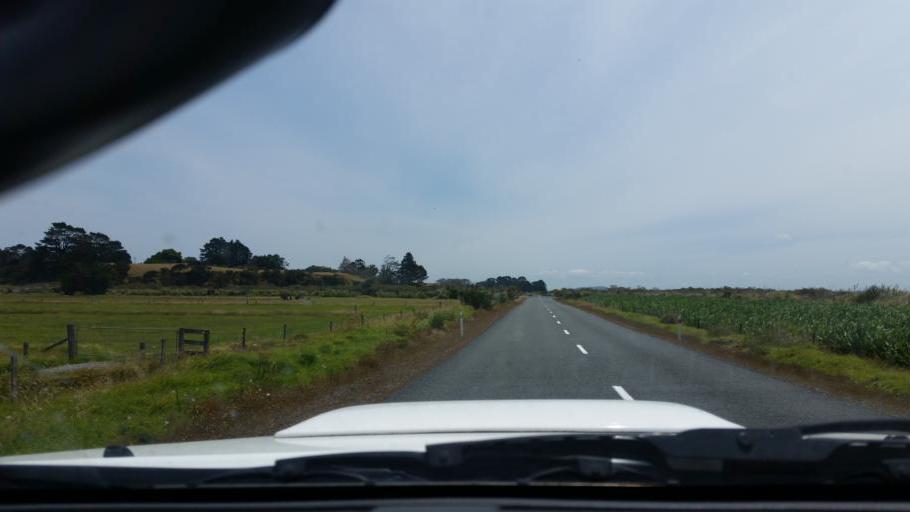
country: NZ
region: Northland
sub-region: Kaipara District
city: Dargaville
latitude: -36.1787
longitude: 174.0294
